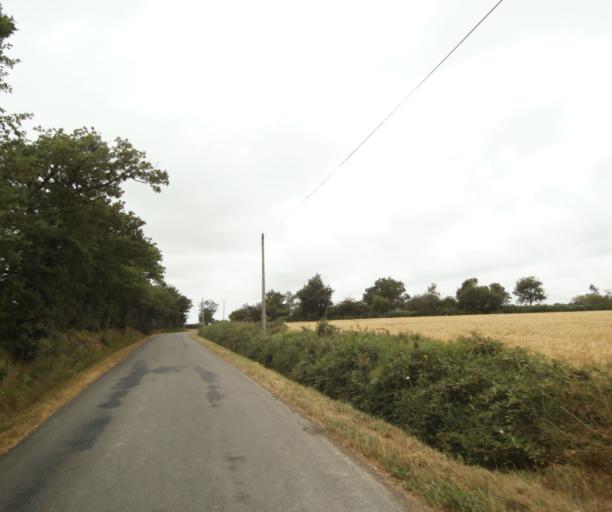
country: FR
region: Pays de la Loire
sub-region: Departement de la Vendee
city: Chateau-d'Olonne
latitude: 46.4956
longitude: -1.6978
